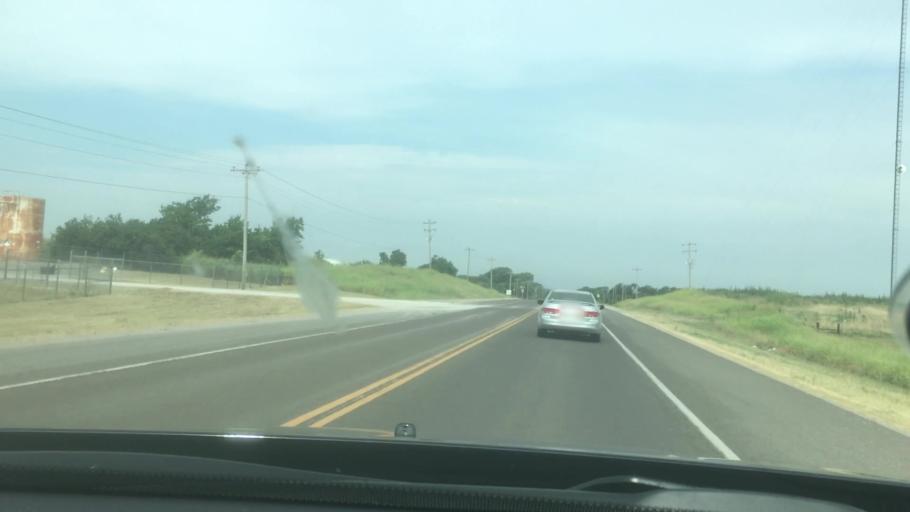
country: US
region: Oklahoma
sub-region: Garvin County
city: Maysville
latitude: 34.8192
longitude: -97.4485
